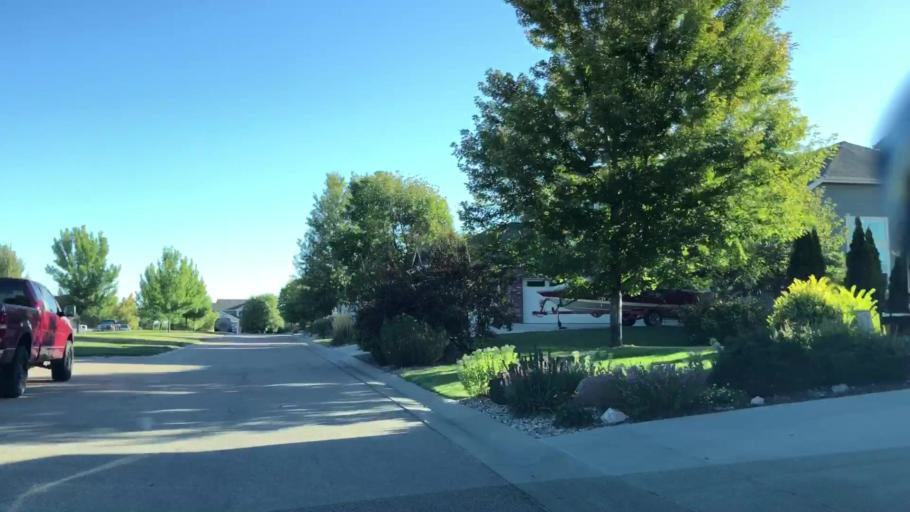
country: US
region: Colorado
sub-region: Larimer County
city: Loveland
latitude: 40.4596
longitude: -105.0346
